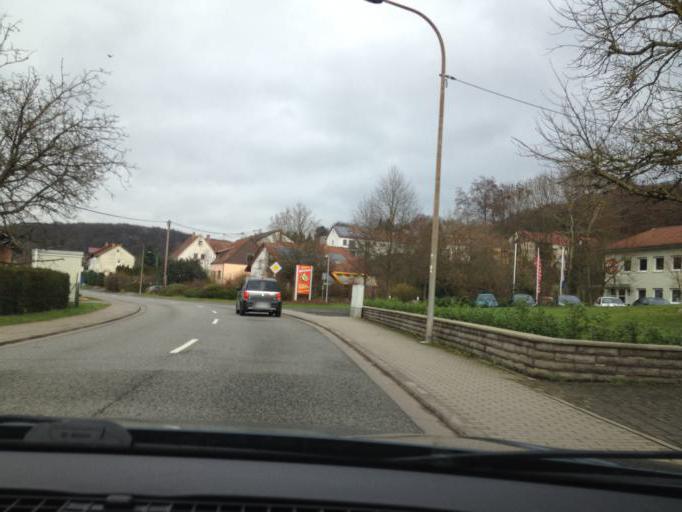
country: DE
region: Saarland
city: Sankt Wendel
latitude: 49.4815
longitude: 7.1803
